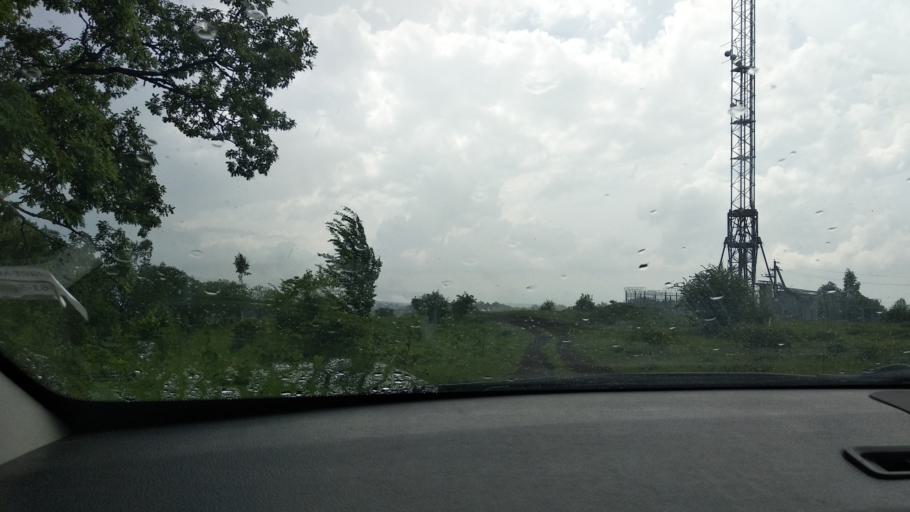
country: RU
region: Adygeya
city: Kamennomostskiy
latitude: 44.2222
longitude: 39.9971
